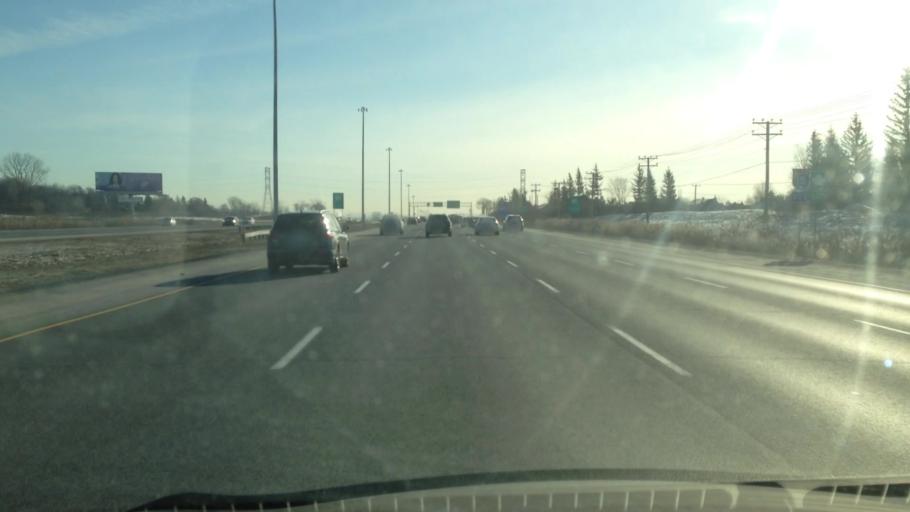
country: CA
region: Quebec
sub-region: Laurentides
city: Blainville
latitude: 45.6506
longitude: -73.8746
